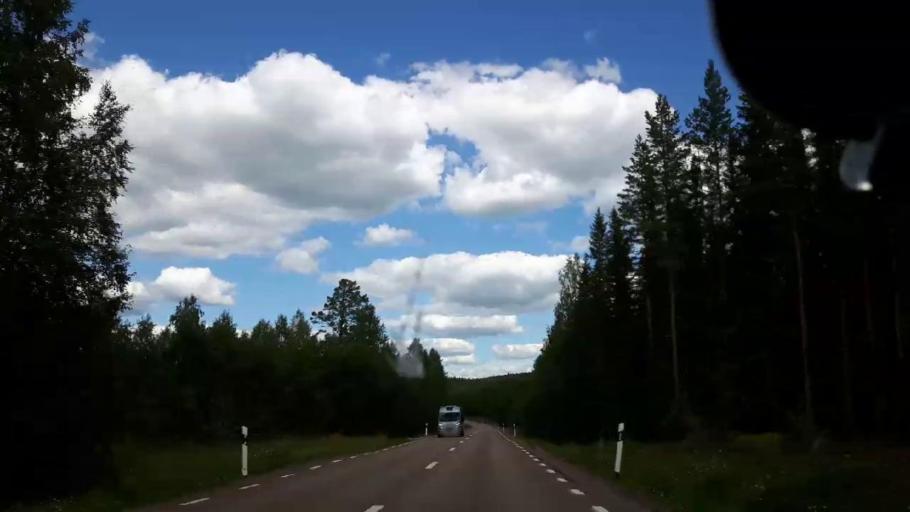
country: SE
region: Jaemtland
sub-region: Ragunda Kommun
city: Hammarstrand
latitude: 62.9149
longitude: 16.7032
